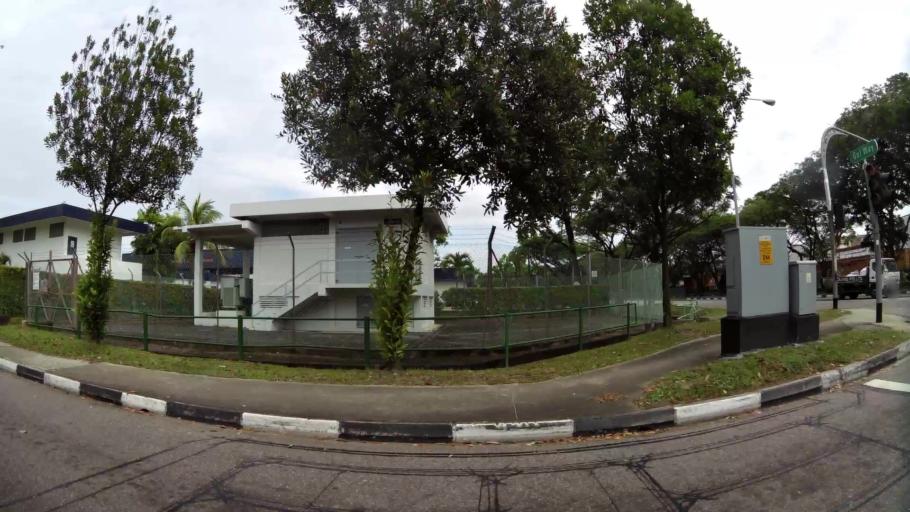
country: MY
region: Johor
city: Johor Bahru
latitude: 1.3200
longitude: 103.6701
